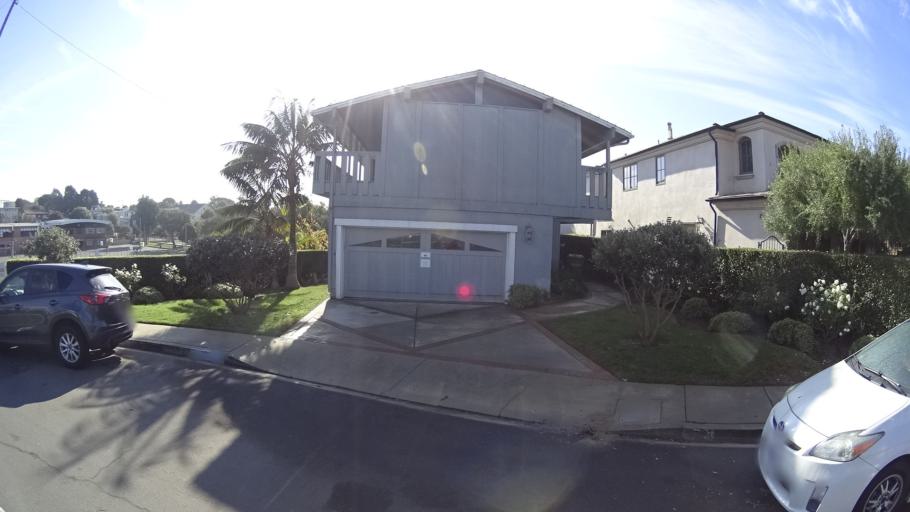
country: US
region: California
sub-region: Los Angeles County
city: Manhattan Beach
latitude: 33.8905
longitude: -118.4060
